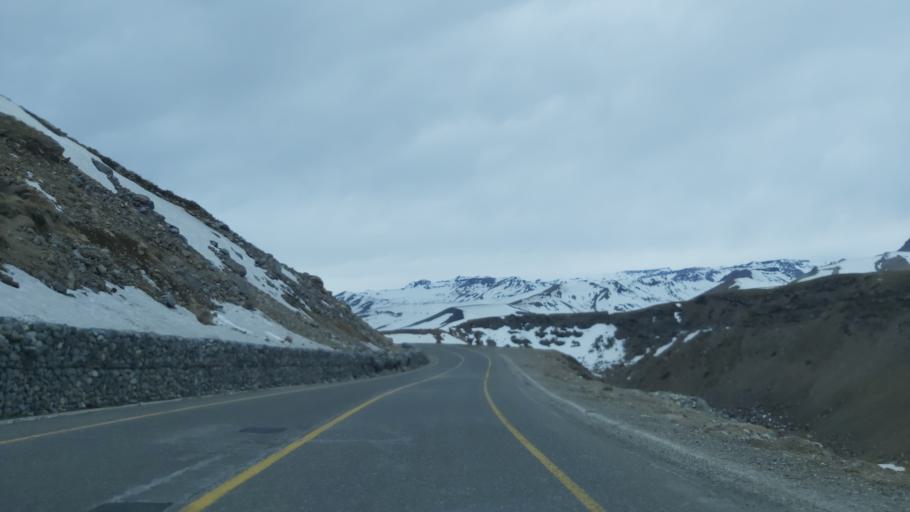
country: CL
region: Maule
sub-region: Provincia de Linares
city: Colbun
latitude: -35.9945
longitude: -70.5592
